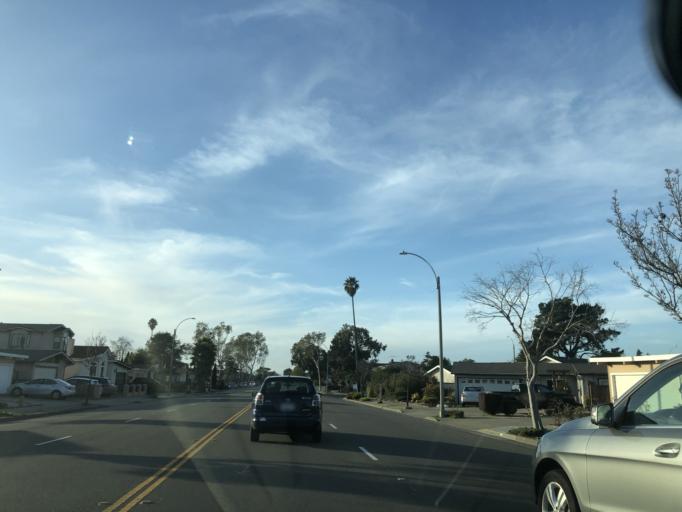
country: US
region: California
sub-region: Alameda County
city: Alameda
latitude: 37.7637
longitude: -122.2638
